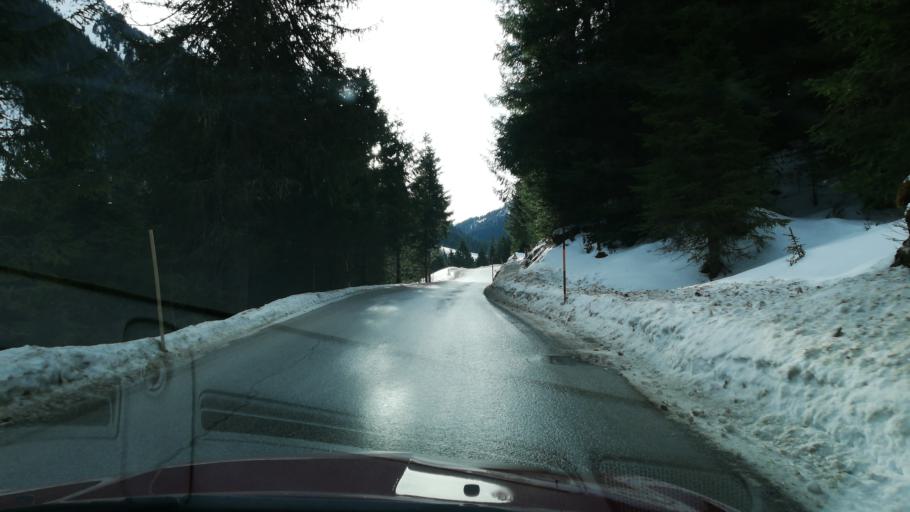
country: AT
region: Styria
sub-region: Politischer Bezirk Liezen
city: Donnersbach
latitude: 47.4241
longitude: 14.1655
